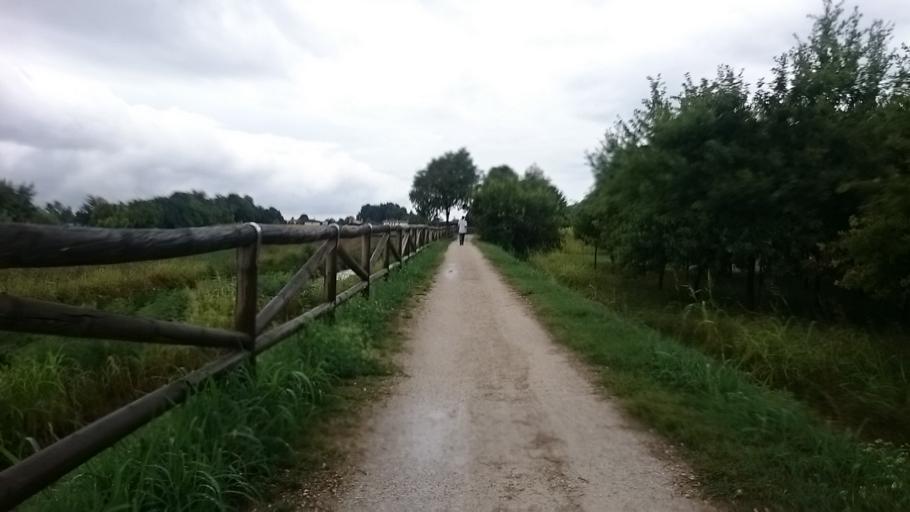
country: IT
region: Veneto
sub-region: Provincia di Treviso
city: Castelfranco Veneto
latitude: 45.6616
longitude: 11.9232
